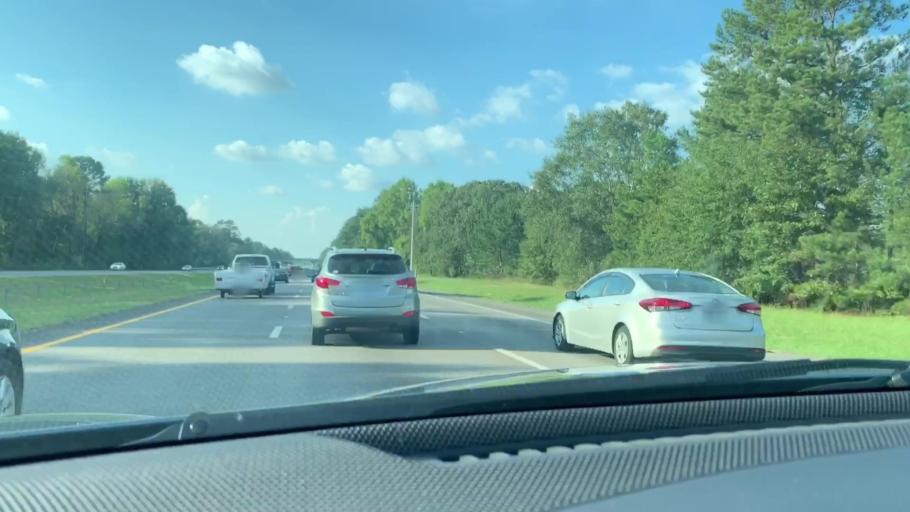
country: US
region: South Carolina
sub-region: Lexington County
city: Pineridge
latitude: 33.8886
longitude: -81.0395
